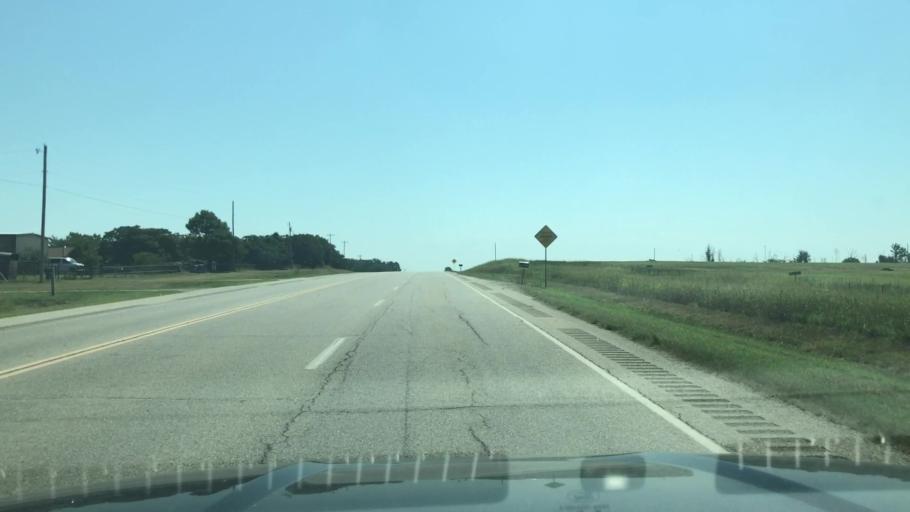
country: US
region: Oklahoma
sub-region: Creek County
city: Mannford
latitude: 36.0030
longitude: -96.4171
